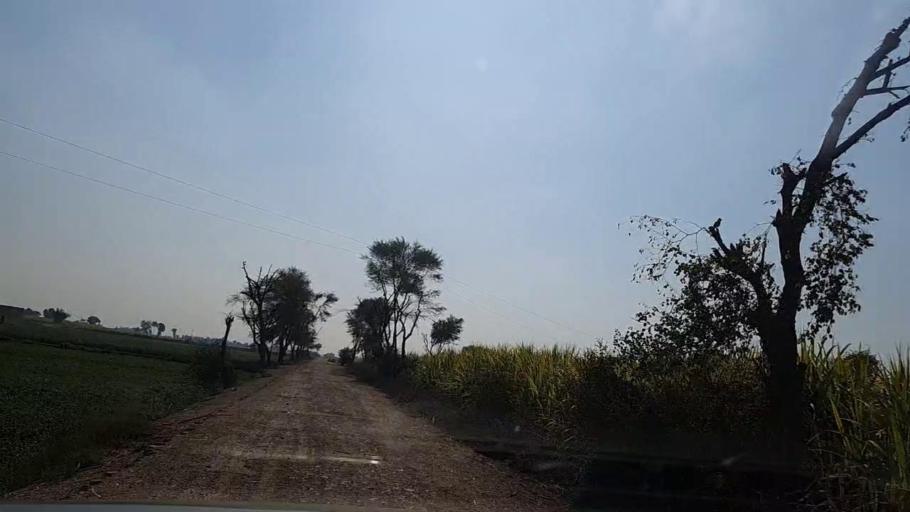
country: PK
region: Sindh
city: Daulatpur
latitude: 26.2874
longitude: 68.0537
